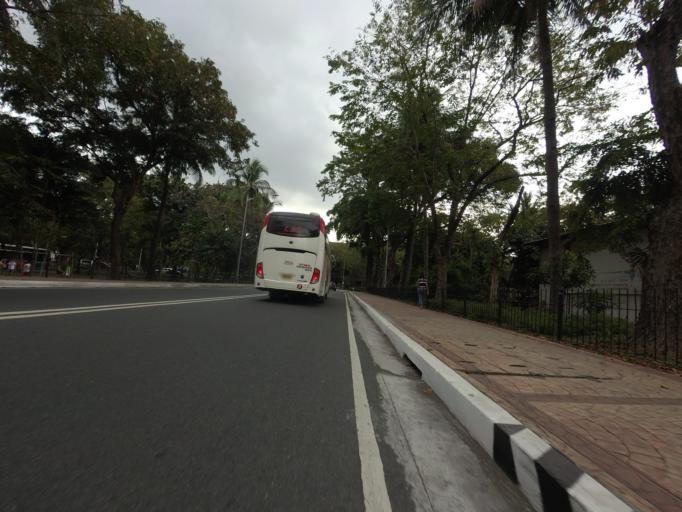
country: PH
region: Metro Manila
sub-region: City of Manila
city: Port Area
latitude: 14.5570
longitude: 120.9824
